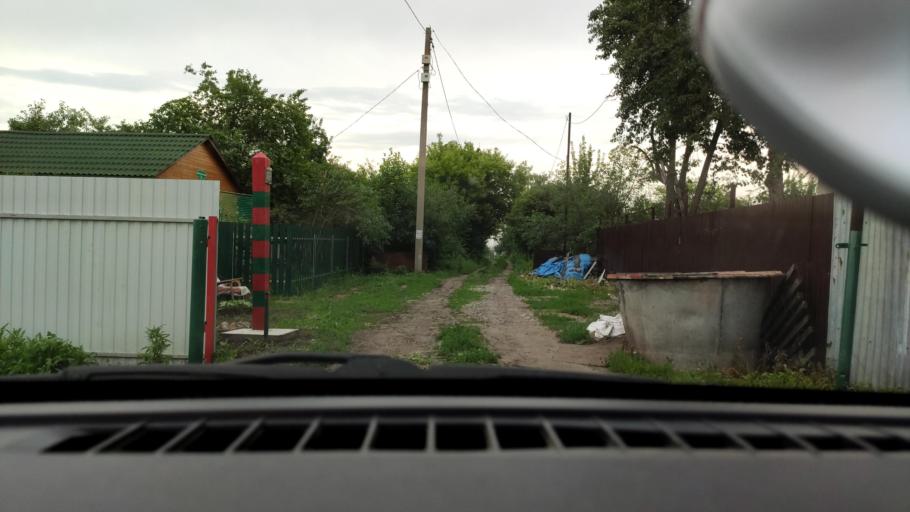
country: RU
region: Samara
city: Petra-Dubrava
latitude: 53.2647
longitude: 50.2922
